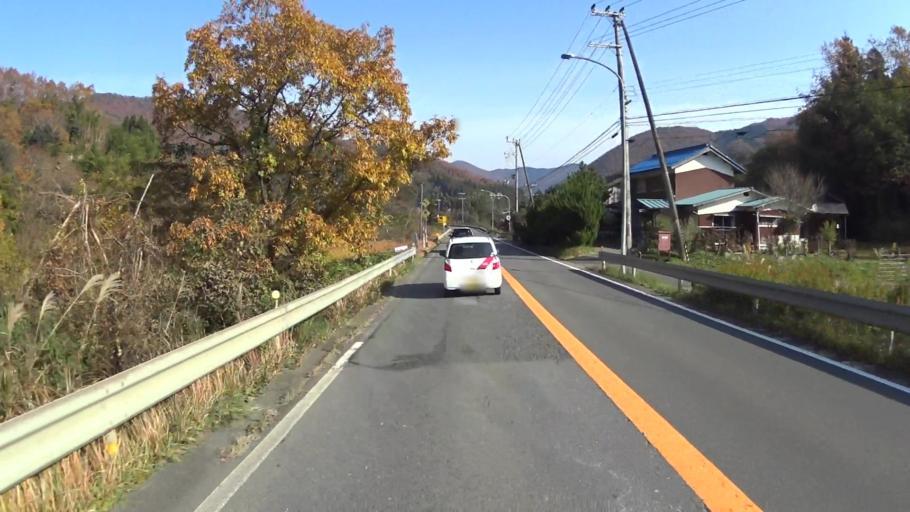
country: JP
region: Kyoto
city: Ayabe
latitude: 35.2051
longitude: 135.2824
